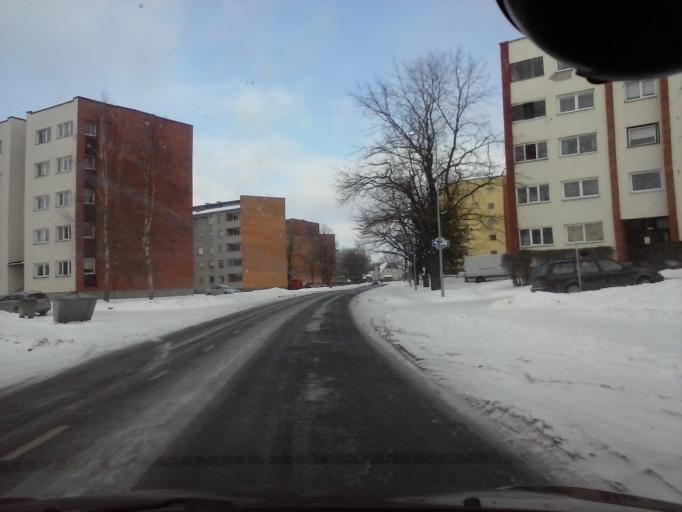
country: EE
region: Viljandimaa
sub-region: Viljandi linn
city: Viljandi
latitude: 58.3565
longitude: 25.5800
